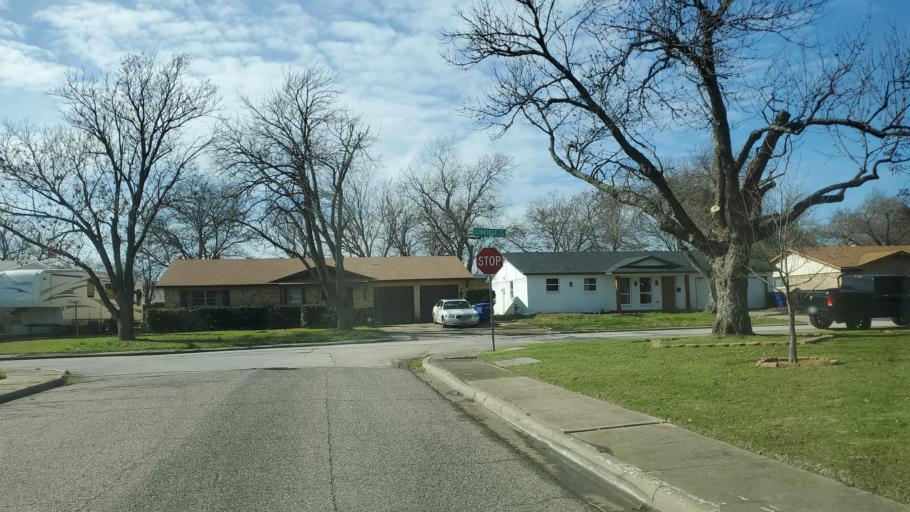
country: US
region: Texas
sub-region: Dallas County
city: Carrollton
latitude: 32.9823
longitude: -96.8871
